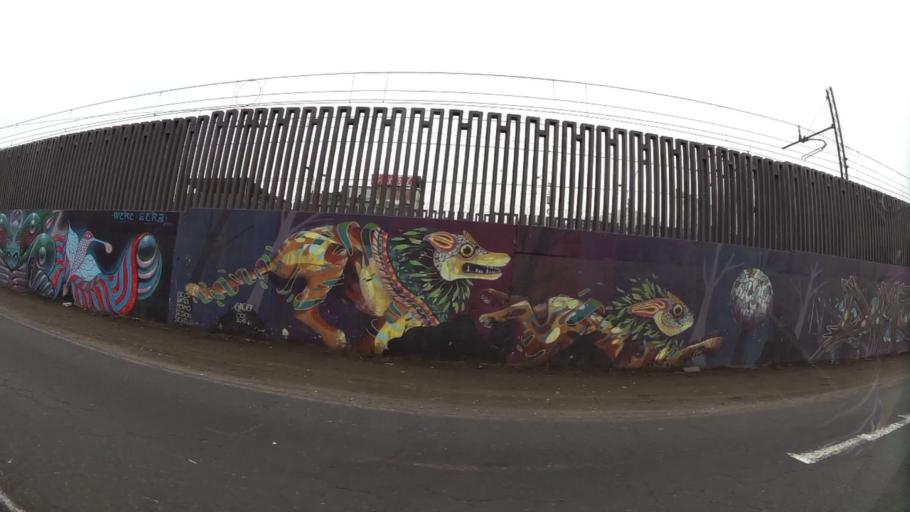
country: PE
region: Lima
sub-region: Lima
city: Surco
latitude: -12.1572
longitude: -76.9640
